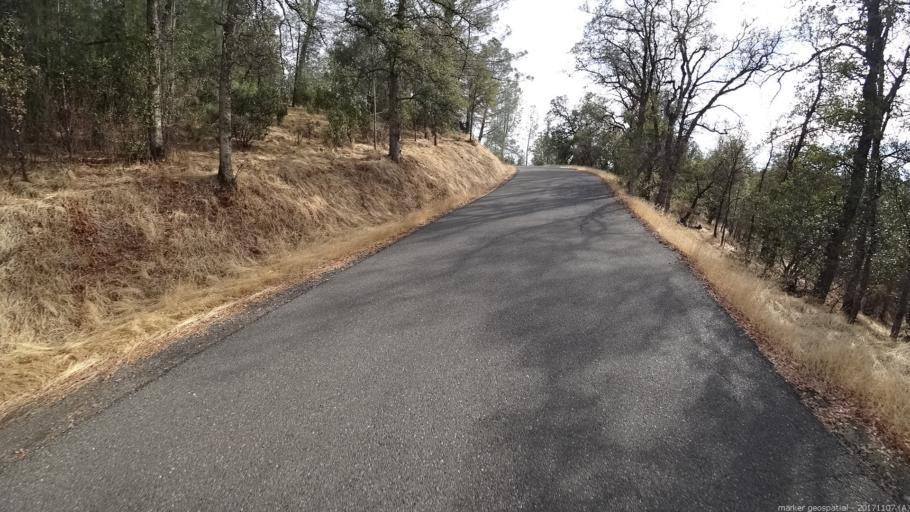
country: US
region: California
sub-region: Shasta County
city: Shasta
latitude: 40.5215
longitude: -122.5262
